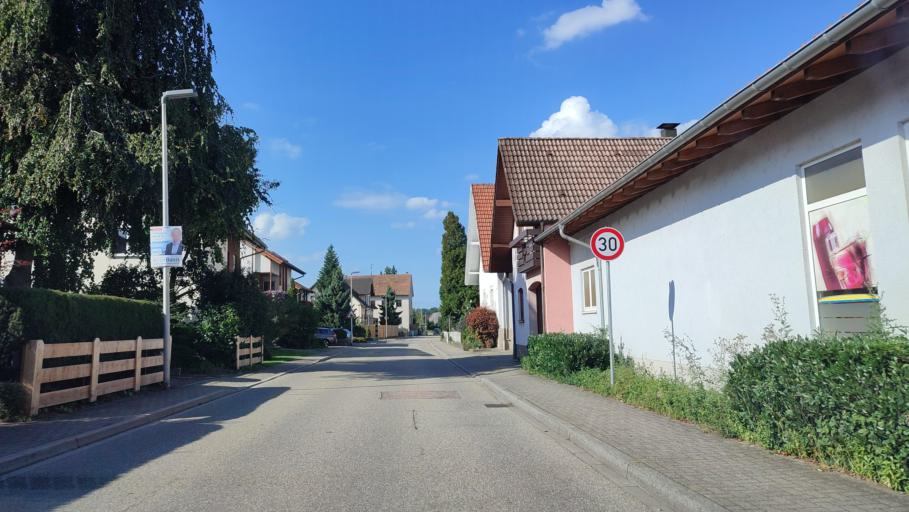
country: DE
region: Baden-Wuerttemberg
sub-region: Freiburg Region
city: Appenweier
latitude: 48.5436
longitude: 8.0182
